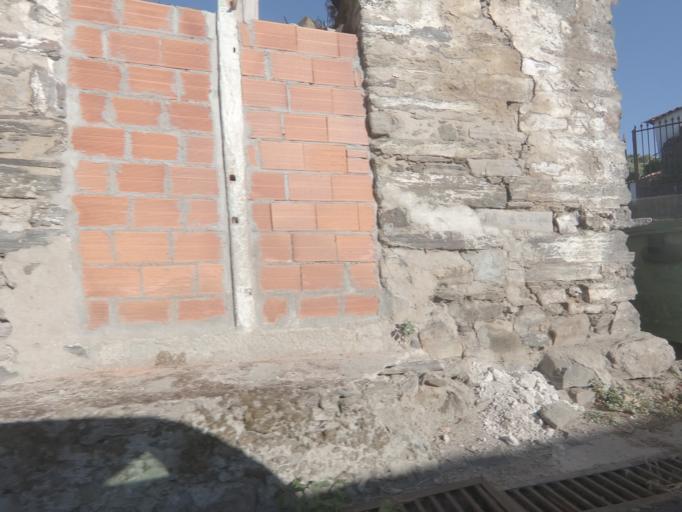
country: PT
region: Vila Real
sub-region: Peso da Regua
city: Peso da Regua
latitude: 41.1894
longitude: -7.7737
